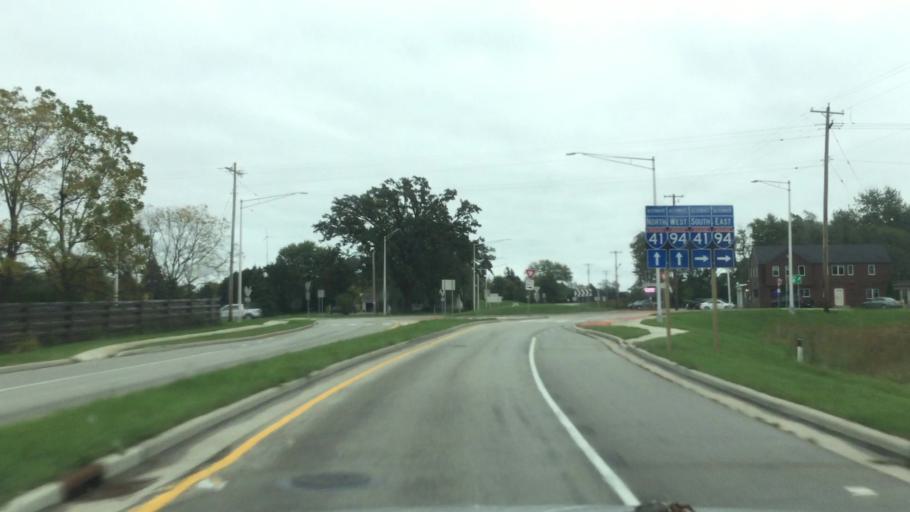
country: US
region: Wisconsin
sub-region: Racine County
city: Eagle Lake
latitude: 42.7419
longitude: -88.1119
